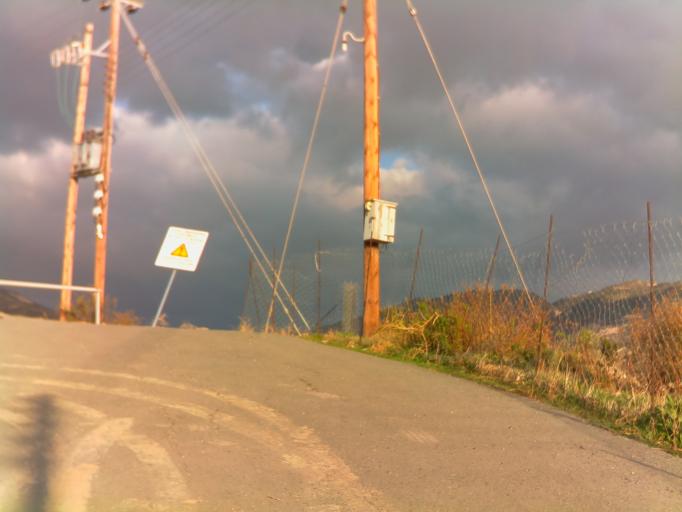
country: CY
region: Pafos
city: Kissonerga
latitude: 34.8545
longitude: 32.4006
